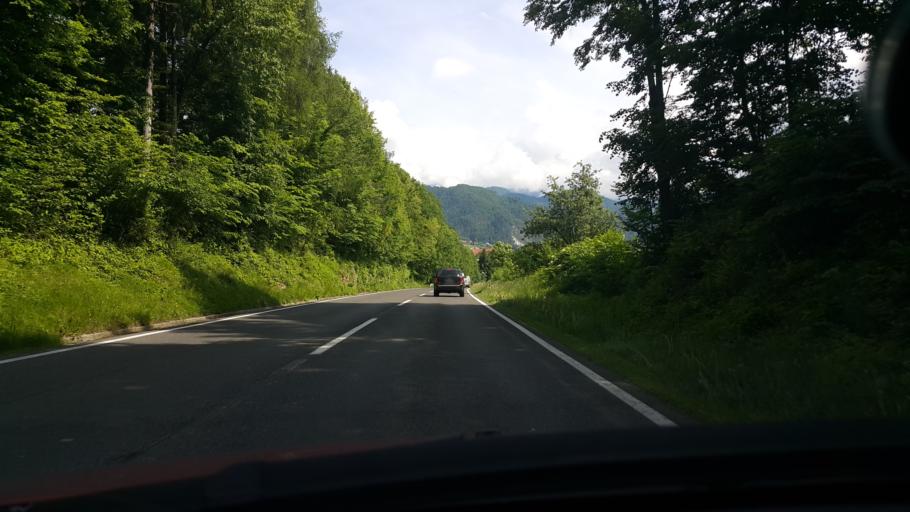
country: SI
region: Trzic
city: Bistrica pri Trzicu
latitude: 46.3345
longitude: 14.2821
